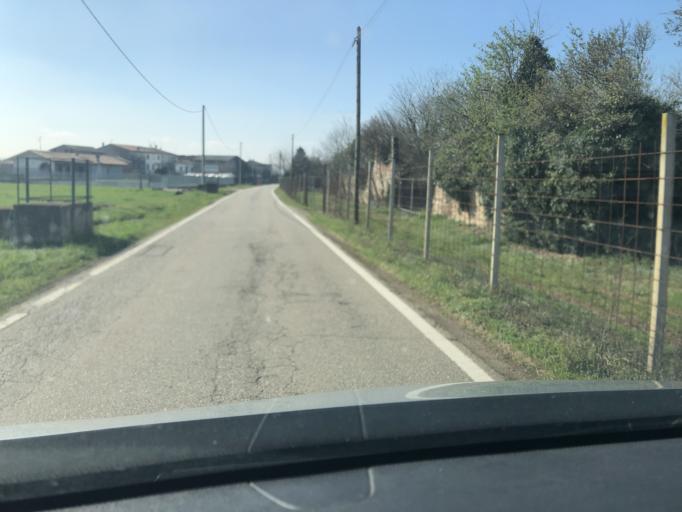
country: IT
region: Veneto
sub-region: Provincia di Verona
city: Sommacampagna
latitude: 45.3828
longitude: 10.8532
